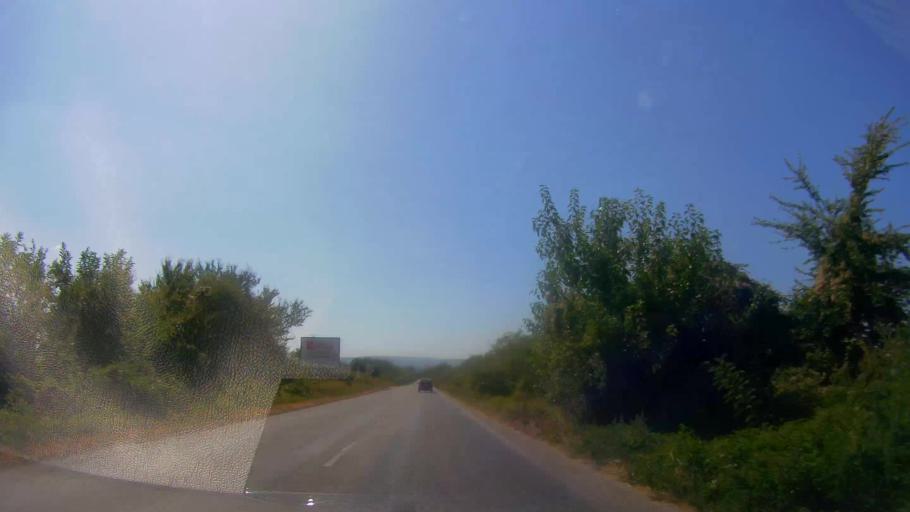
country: BG
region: Veliko Turnovo
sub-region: Obshtina Gorna Oryakhovitsa
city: Purvomaytsi
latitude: 43.2257
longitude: 25.6381
